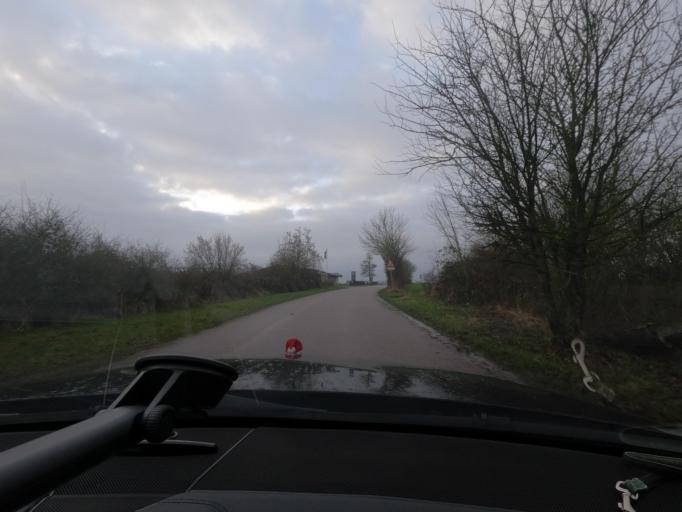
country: DK
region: South Denmark
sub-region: Sonderborg Kommune
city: Horuphav
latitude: 54.8752
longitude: 10.0095
